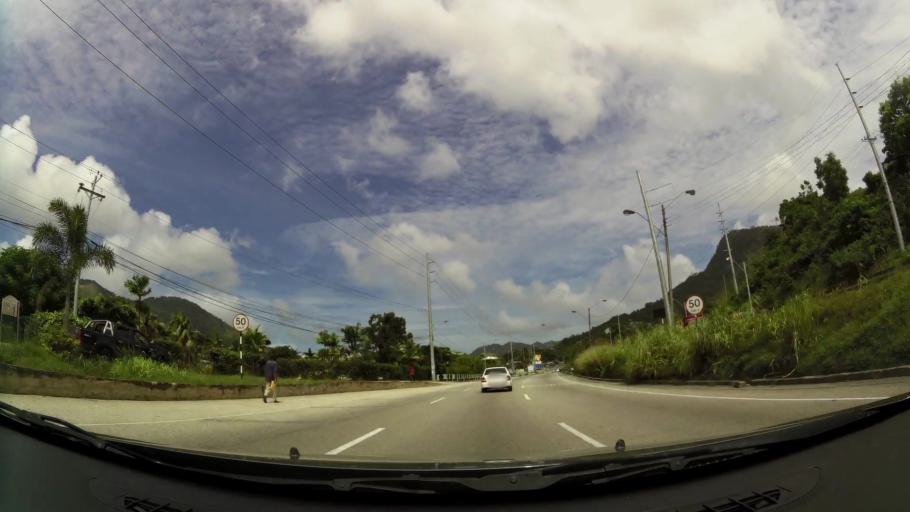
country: TT
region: City of Port of Spain
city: Mucurapo
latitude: 10.6823
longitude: -61.5532
